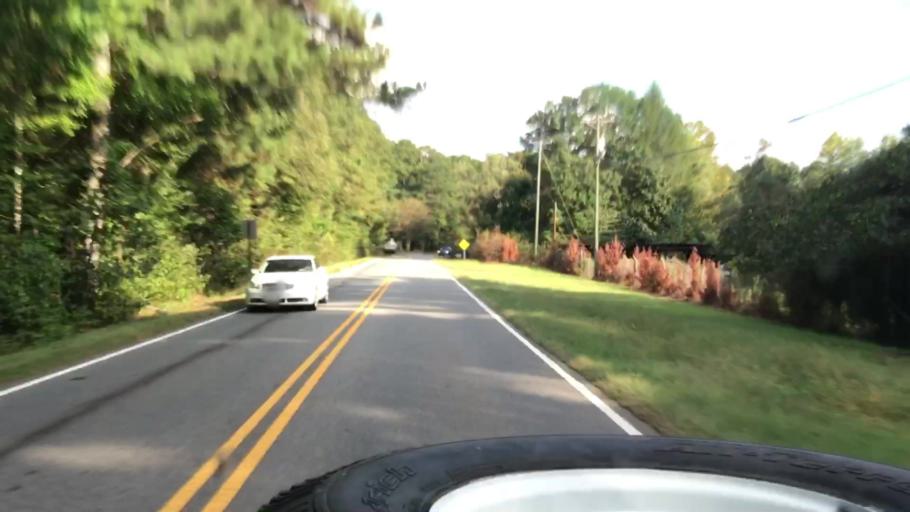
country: US
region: Georgia
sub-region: Forsyth County
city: Cumming
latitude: 34.1788
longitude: -84.0840
